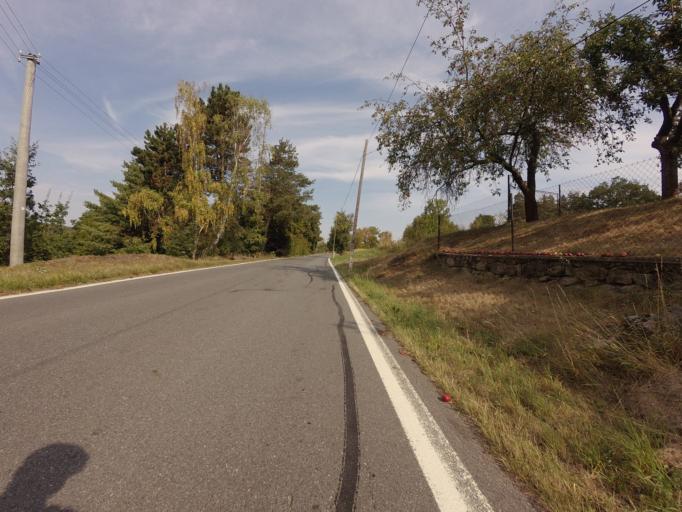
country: CZ
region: Central Bohemia
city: Petrovice
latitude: 49.5422
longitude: 14.3482
